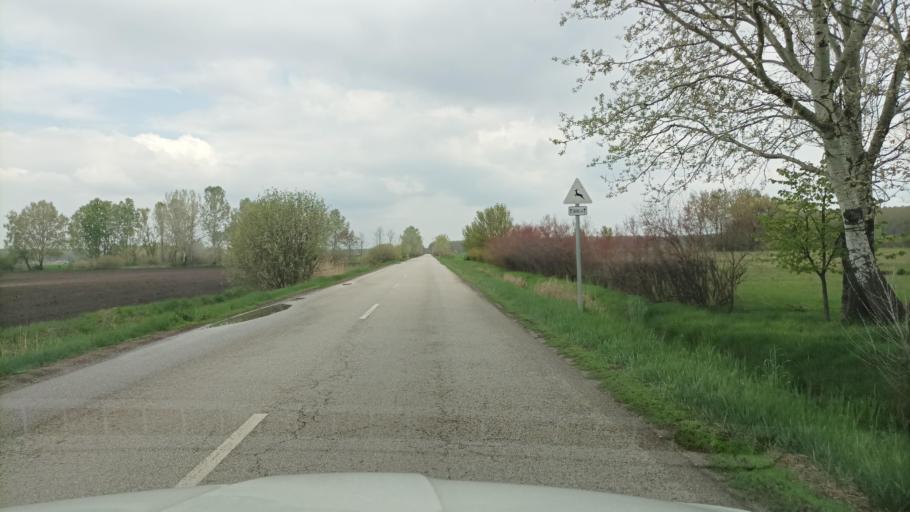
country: HU
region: Pest
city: Kocser
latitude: 47.0047
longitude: 19.9242
